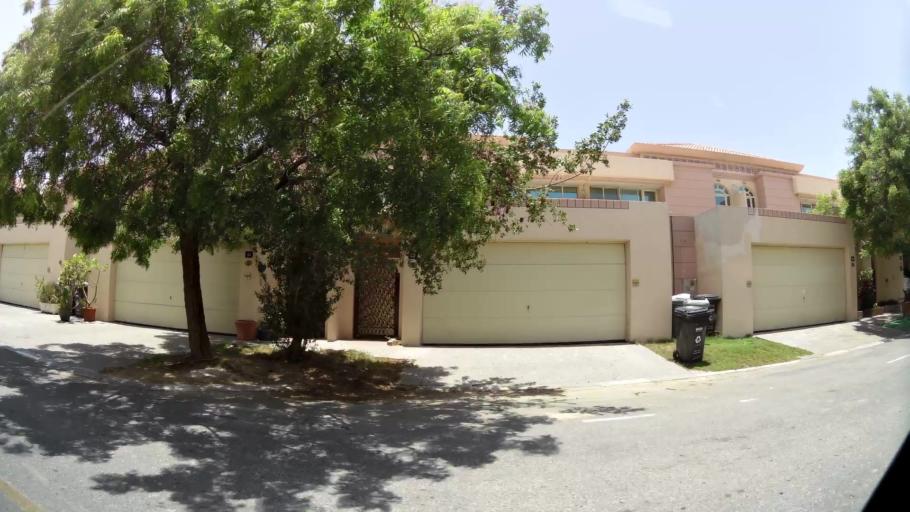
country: AE
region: Dubai
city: Dubai
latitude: 25.1709
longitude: 55.2387
